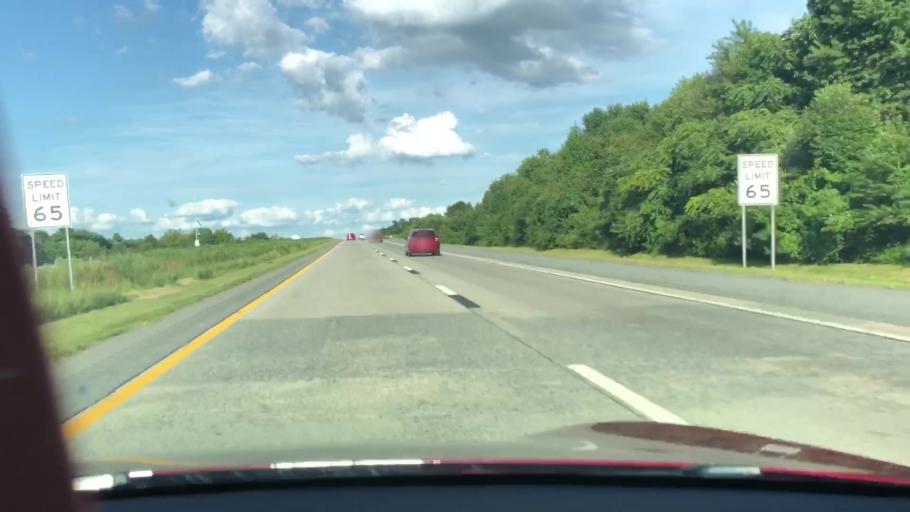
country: US
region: Delaware
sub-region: New Castle County
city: Middletown
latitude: 39.4614
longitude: -75.6629
